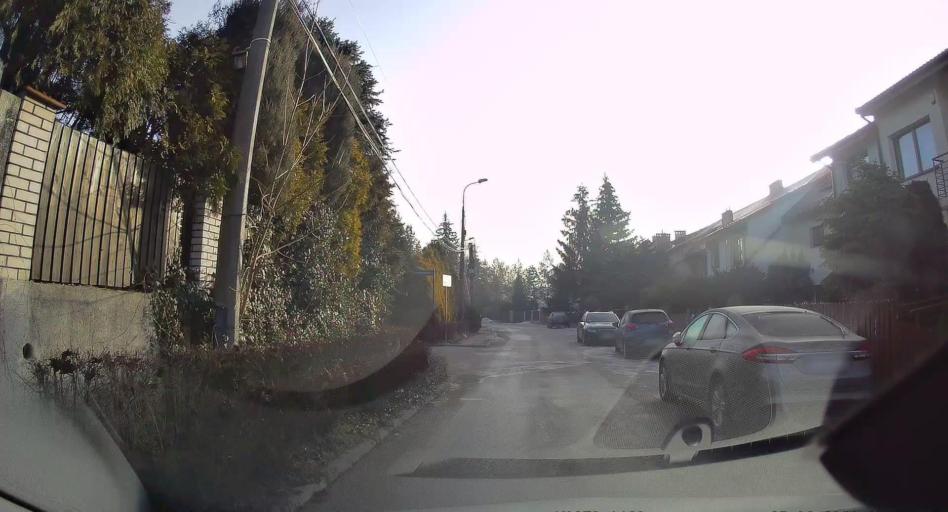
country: PL
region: Lesser Poland Voivodeship
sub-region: Powiat krakowski
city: Libertow
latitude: 49.9975
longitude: 19.9089
